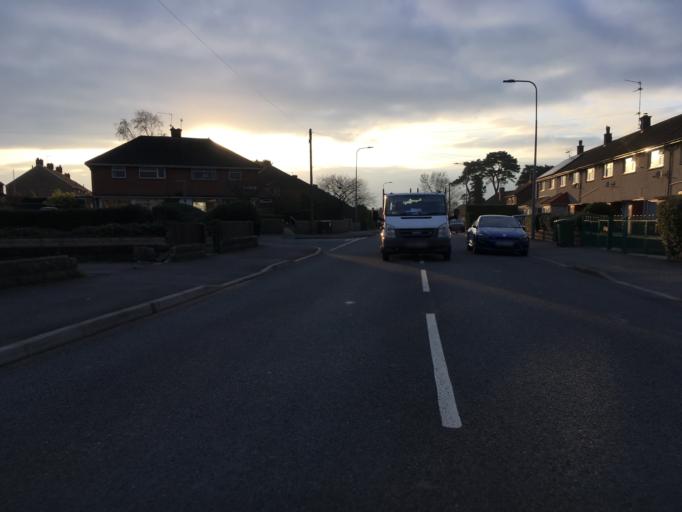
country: GB
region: Wales
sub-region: Newport
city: Marshfield
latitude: 51.5287
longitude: -3.1219
